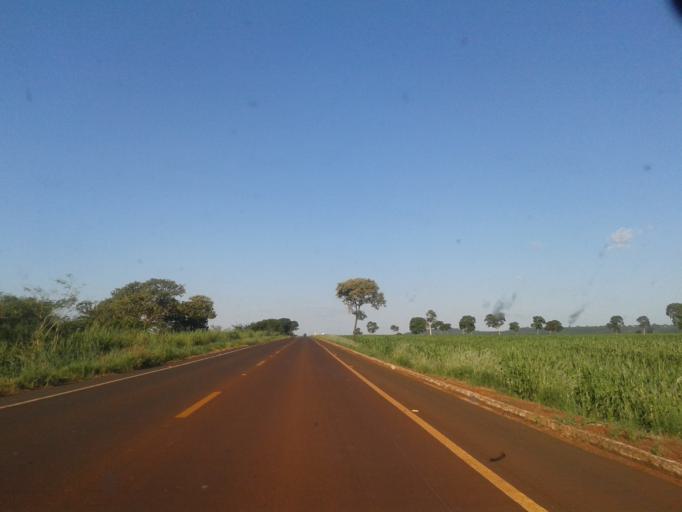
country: BR
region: Minas Gerais
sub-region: Capinopolis
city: Capinopolis
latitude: -18.7122
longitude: -49.8387
